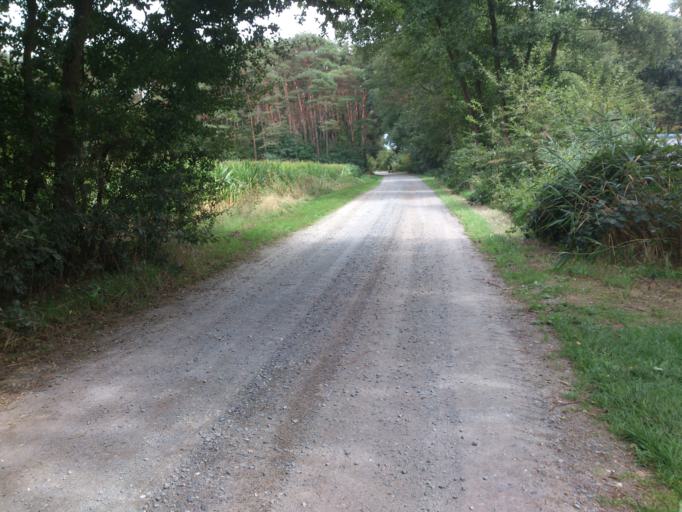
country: BE
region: Flanders
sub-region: Provincie Antwerpen
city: Mol
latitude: 51.2109
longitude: 5.0945
